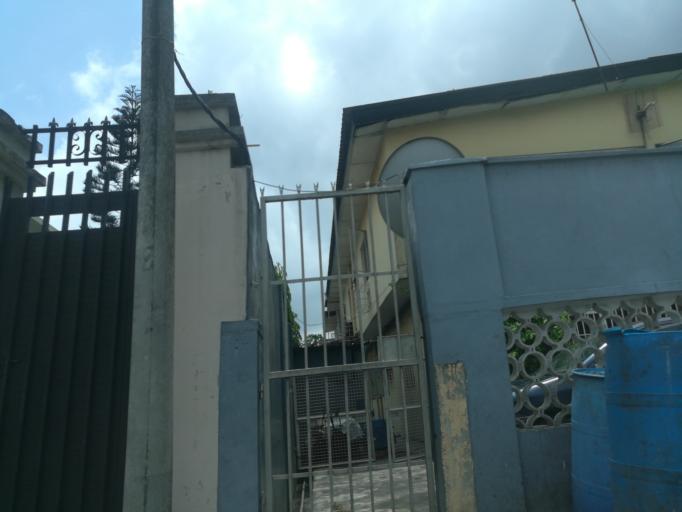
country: NG
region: Lagos
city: Somolu
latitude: 6.5515
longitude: 3.3630
